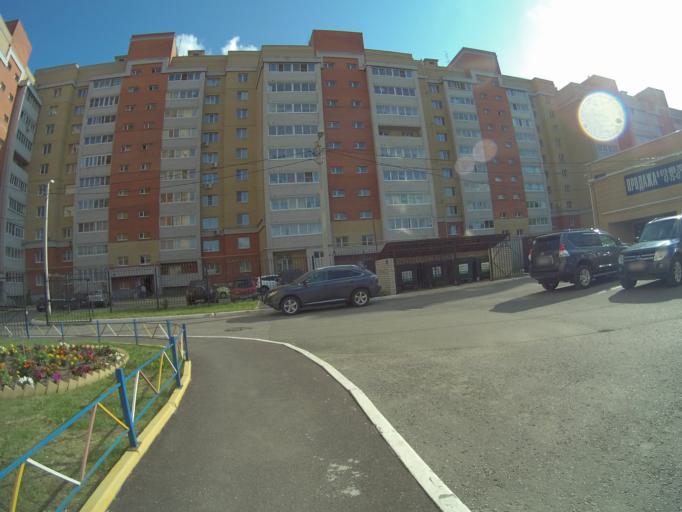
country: RU
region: Vladimir
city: Vladimir
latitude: 56.1378
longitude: 40.3830
